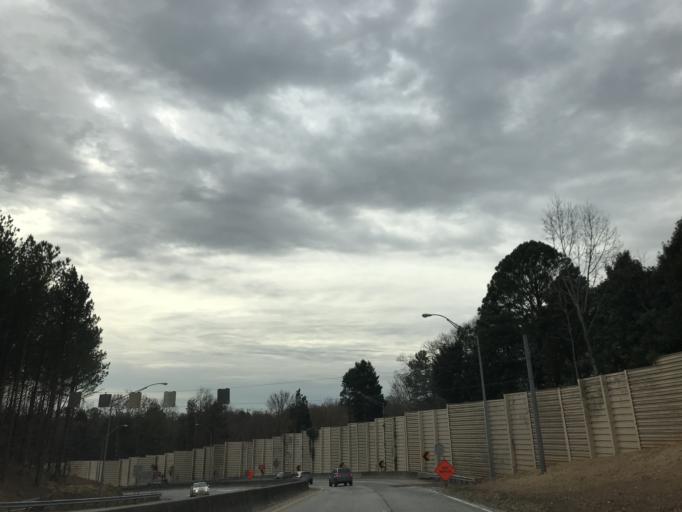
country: US
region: Georgia
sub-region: Fulton County
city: Sandy Springs
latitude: 33.9034
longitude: -84.3612
